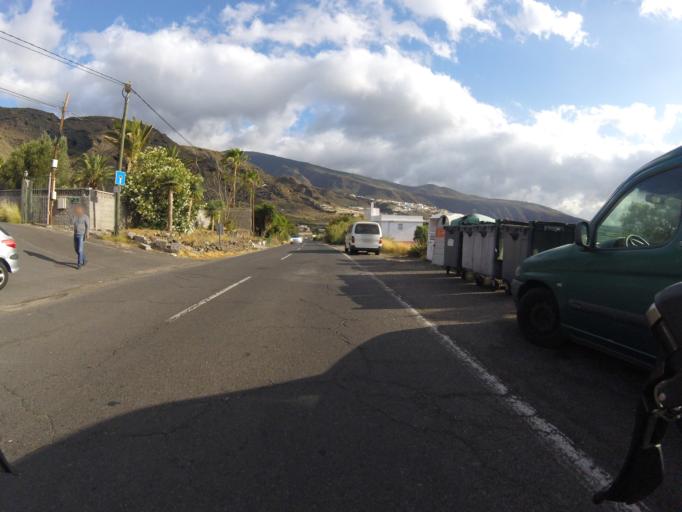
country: ES
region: Canary Islands
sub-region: Provincia de Santa Cruz de Tenerife
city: Candelaria
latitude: 28.3660
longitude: -16.3744
